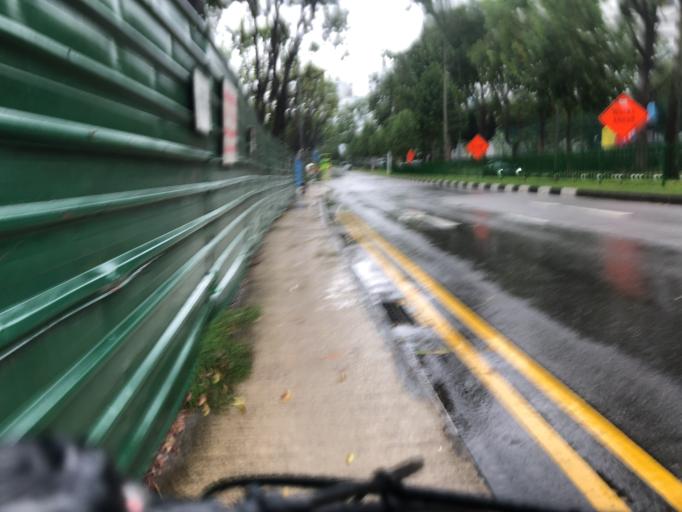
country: SG
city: Singapore
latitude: 1.3421
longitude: 103.7590
